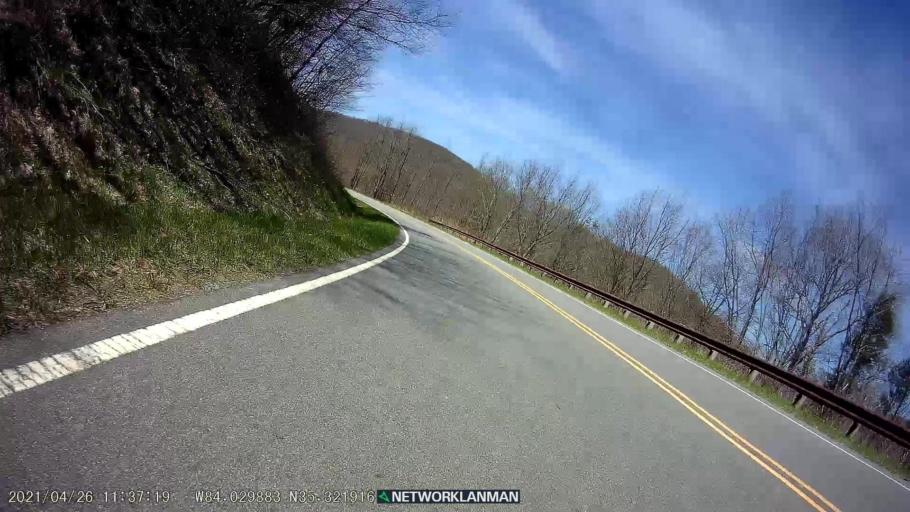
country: US
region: North Carolina
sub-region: Graham County
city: Robbinsville
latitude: 35.3216
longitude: -84.0298
